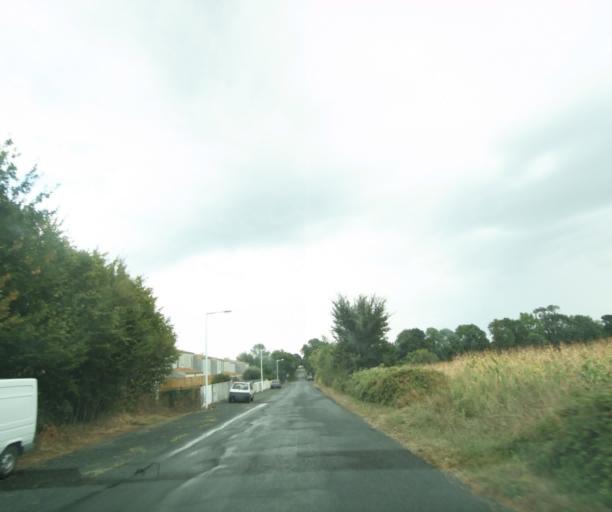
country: FR
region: Poitou-Charentes
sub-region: Departement de la Charente-Maritime
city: Tonnay-Charente
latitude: 45.9429
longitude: -0.8793
